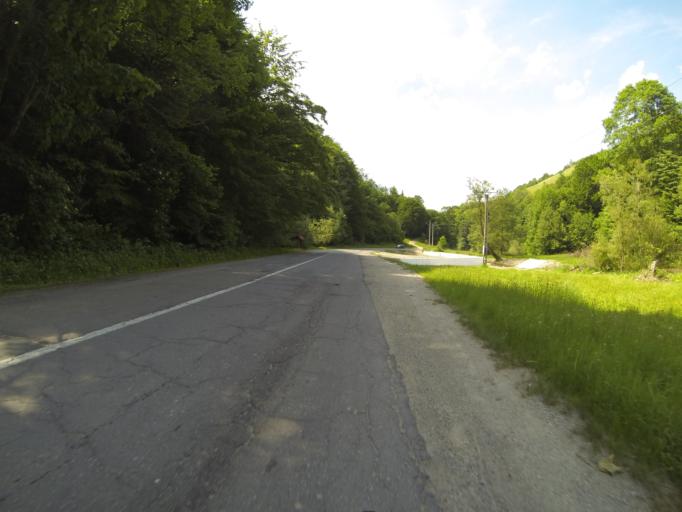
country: RO
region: Brasov
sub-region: Comuna Poiana Marului
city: Poiana Marului
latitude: 45.6240
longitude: 25.2871
